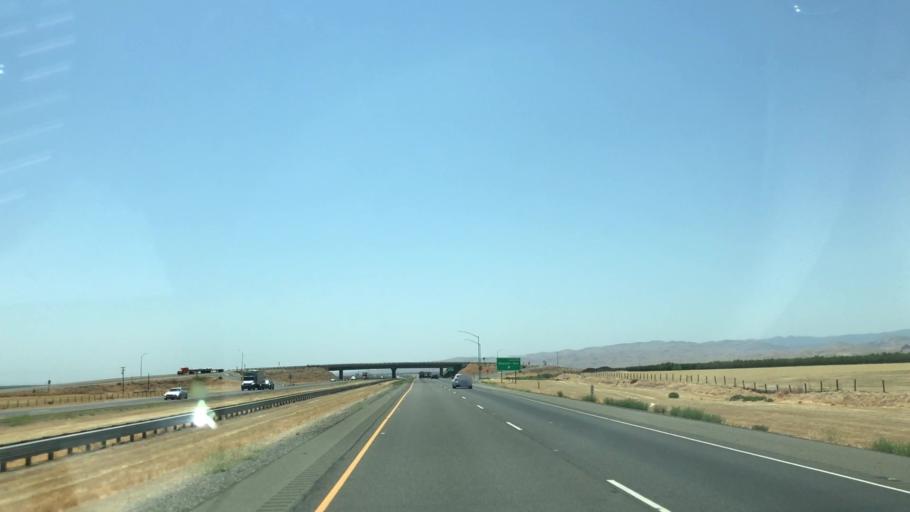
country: US
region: California
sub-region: Fresno County
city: Firebaugh
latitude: 36.6894
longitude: -120.6613
